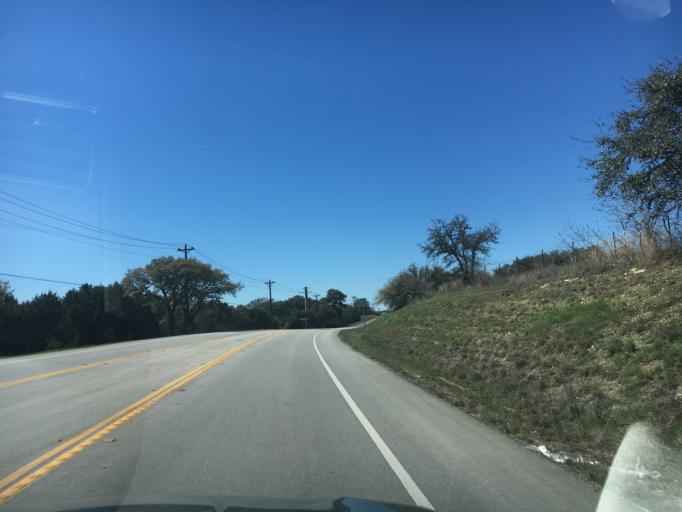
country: US
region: Texas
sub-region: Travis County
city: The Hills
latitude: 30.2907
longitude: -98.0209
